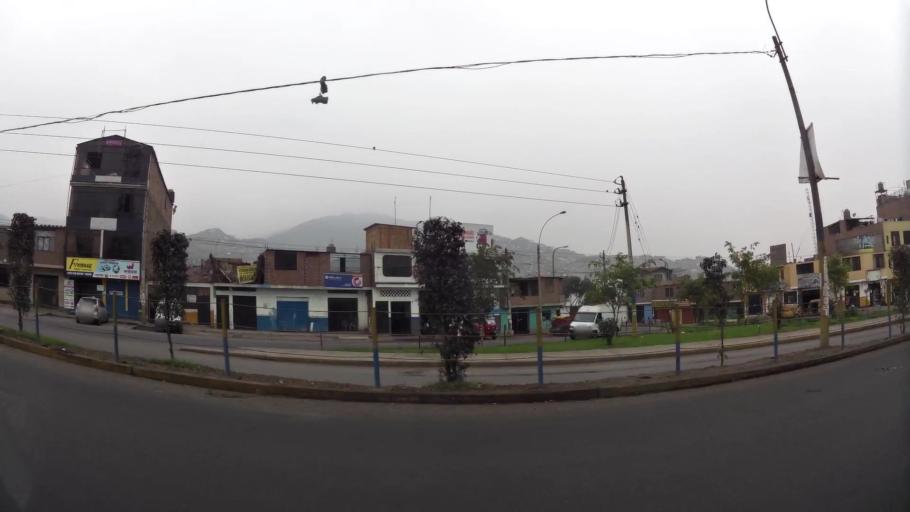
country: PE
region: Lima
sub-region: Lima
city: Urb. Santo Domingo
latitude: -11.9388
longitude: -76.9724
